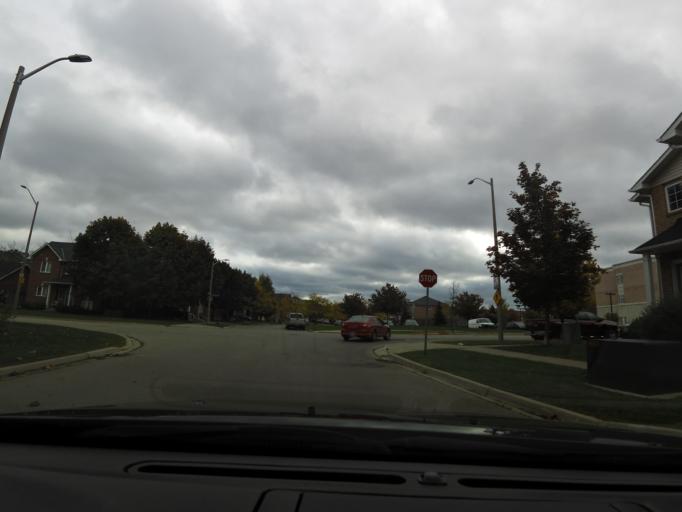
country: CA
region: Ontario
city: Burlington
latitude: 43.3940
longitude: -79.7805
